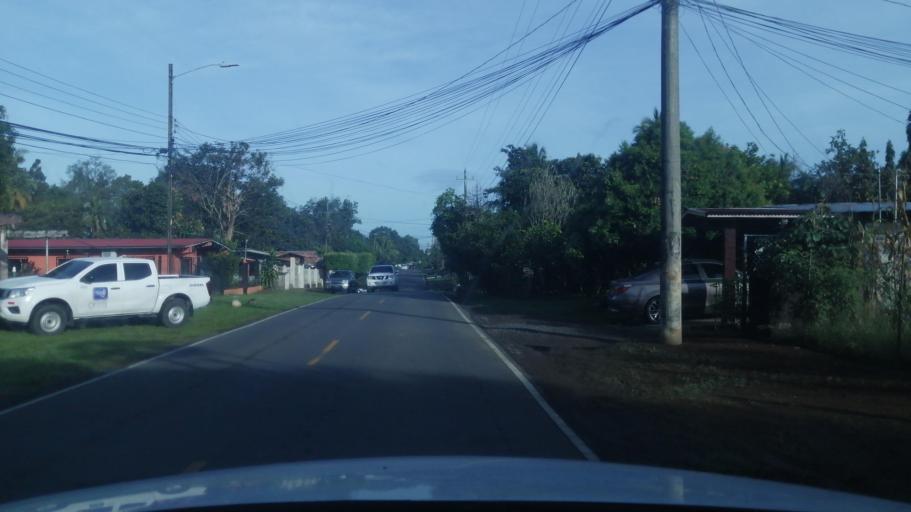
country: PA
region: Chiriqui
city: David
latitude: 8.4252
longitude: -82.4393
